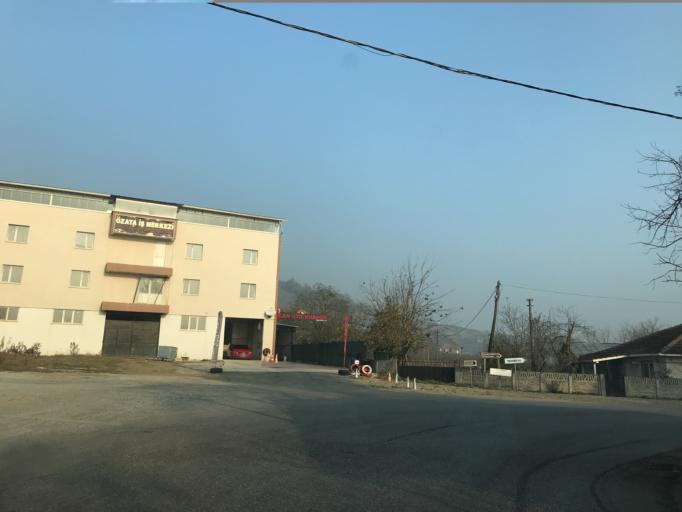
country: TR
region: Duzce
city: Cumayeri
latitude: 40.8837
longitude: 30.9514
